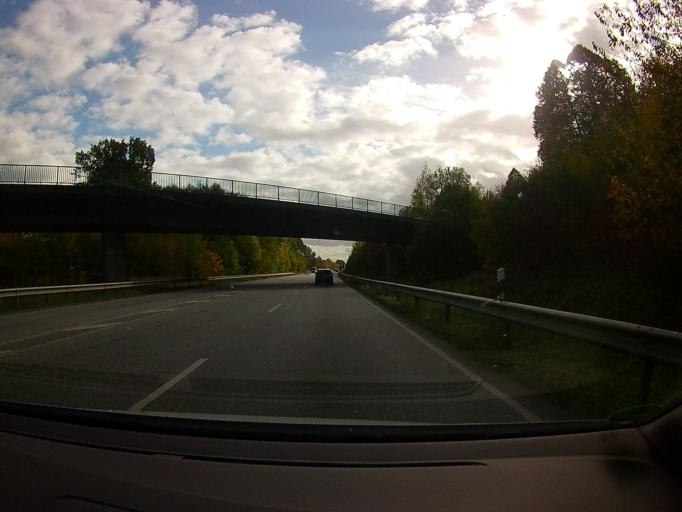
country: DE
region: Schleswig-Holstein
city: Kuddeworde
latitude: 53.5838
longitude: 10.3960
